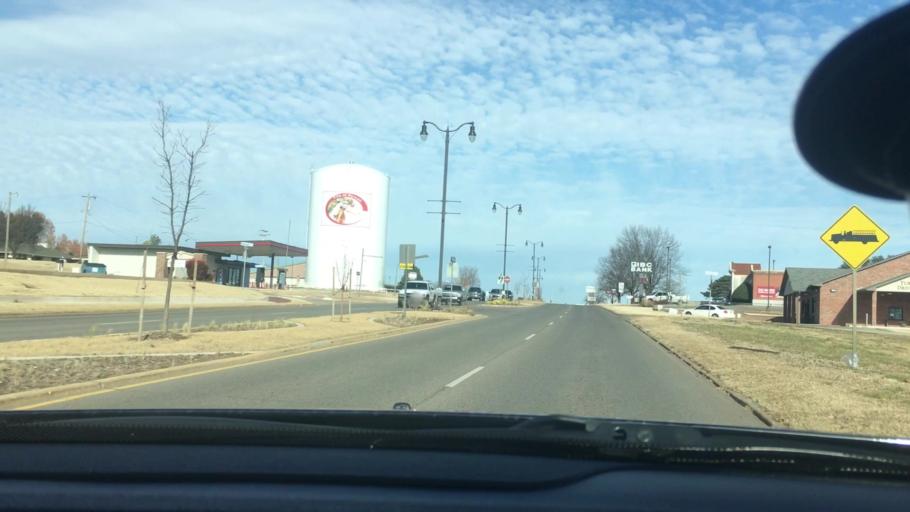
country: US
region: Oklahoma
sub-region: McClain County
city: Purcell
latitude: 35.0263
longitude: -97.3655
